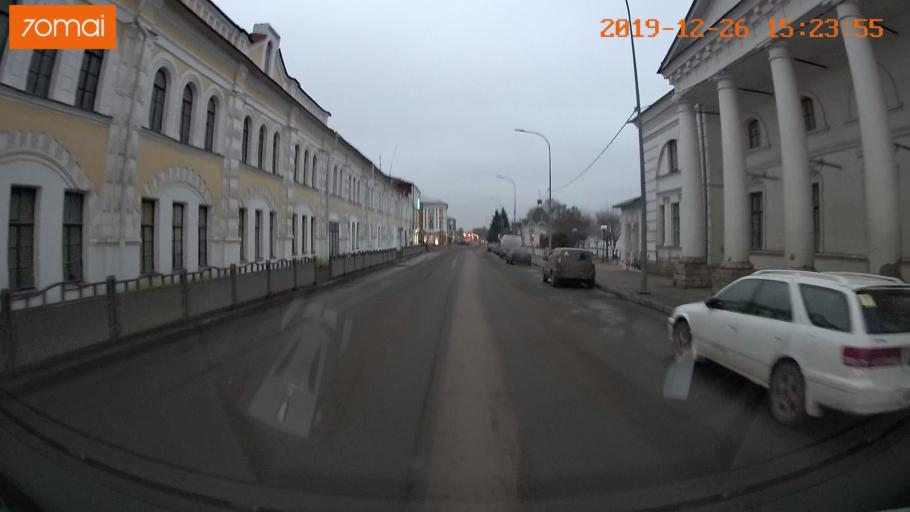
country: RU
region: Jaroslavl
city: Rybinsk
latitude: 58.0496
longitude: 38.8548
